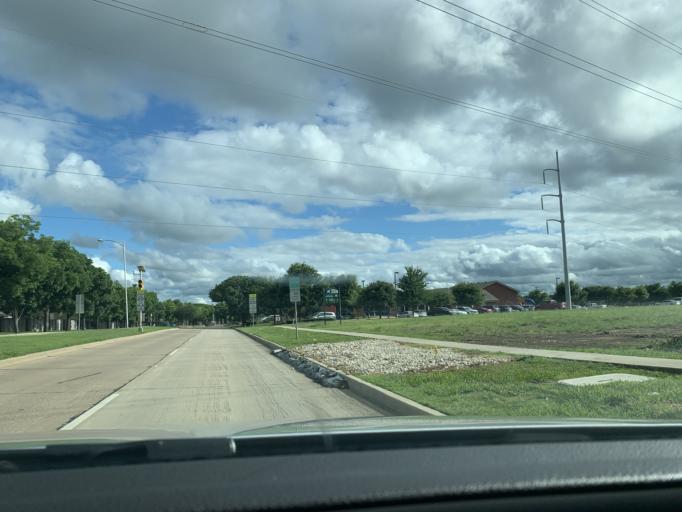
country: US
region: Texas
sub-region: Dallas County
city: Grand Prairie
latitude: 32.6627
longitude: -97.0025
